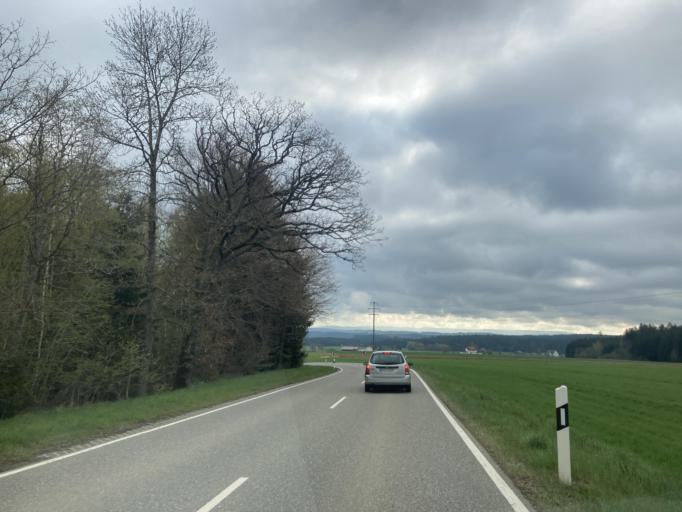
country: DE
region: Baden-Wuerttemberg
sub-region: Freiburg Region
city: Unterkirnach
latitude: 48.0270
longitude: 8.3951
